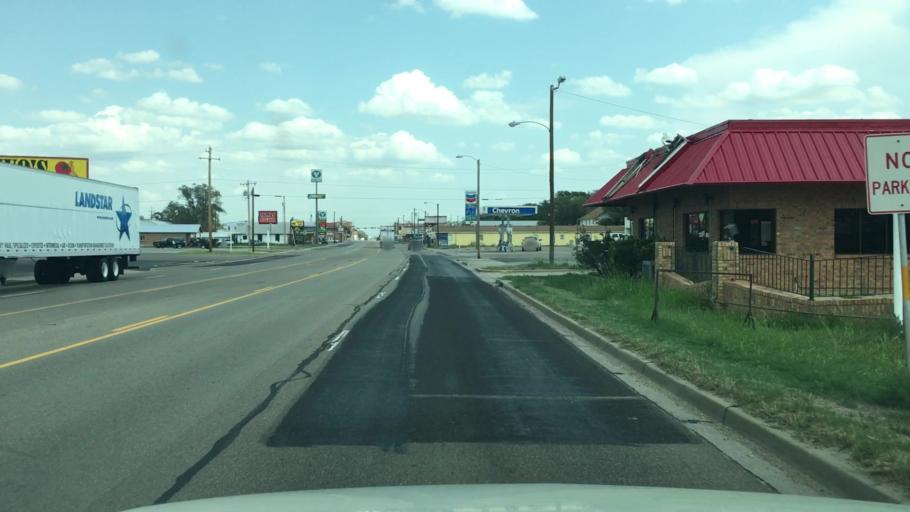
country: US
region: Texas
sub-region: Donley County
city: Clarendon
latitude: 34.9402
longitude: -100.8930
